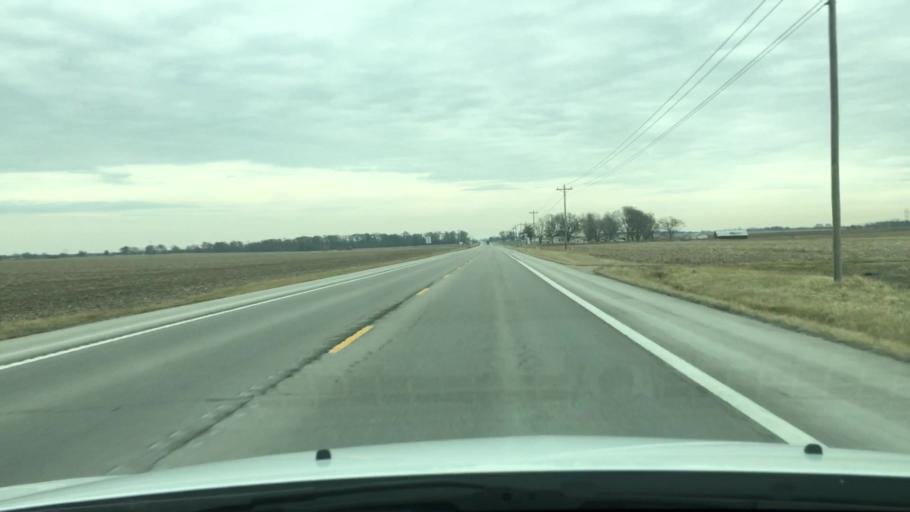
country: US
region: Missouri
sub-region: Audrain County
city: Mexico
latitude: 39.1639
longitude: -91.7672
